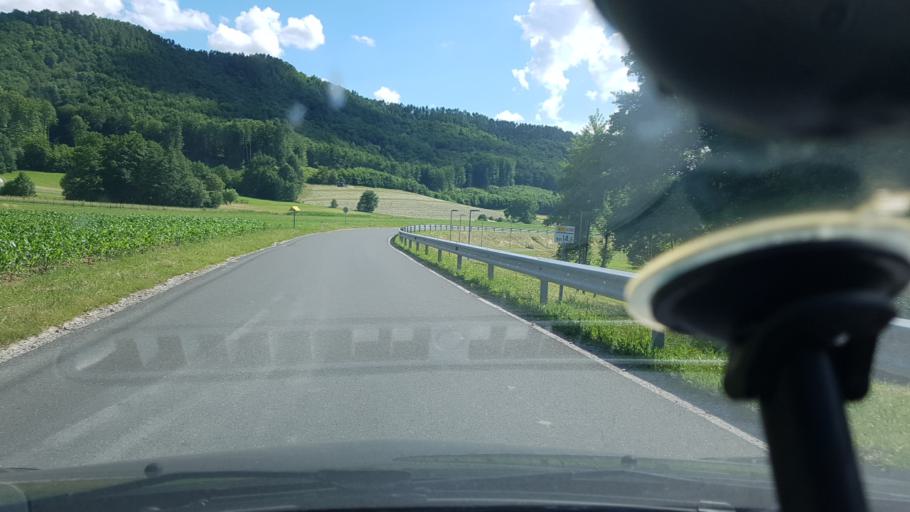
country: SI
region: Rogatec
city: Rogatec
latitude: 46.2401
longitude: 15.7129
